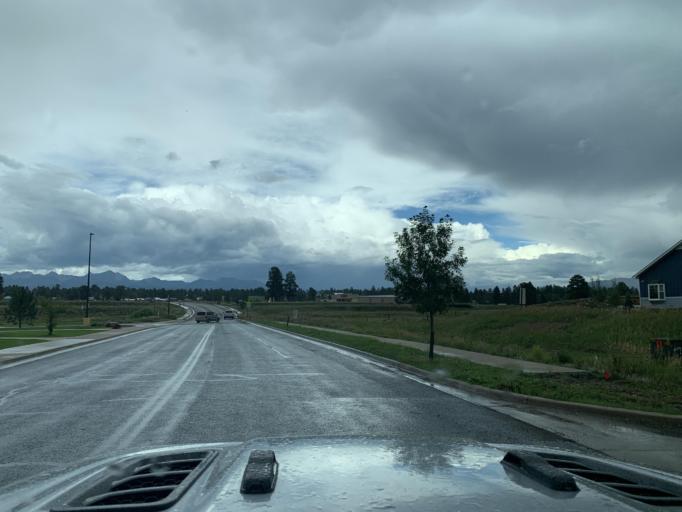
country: US
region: Colorado
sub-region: Archuleta County
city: Pagosa Springs
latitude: 37.2596
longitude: -107.0618
